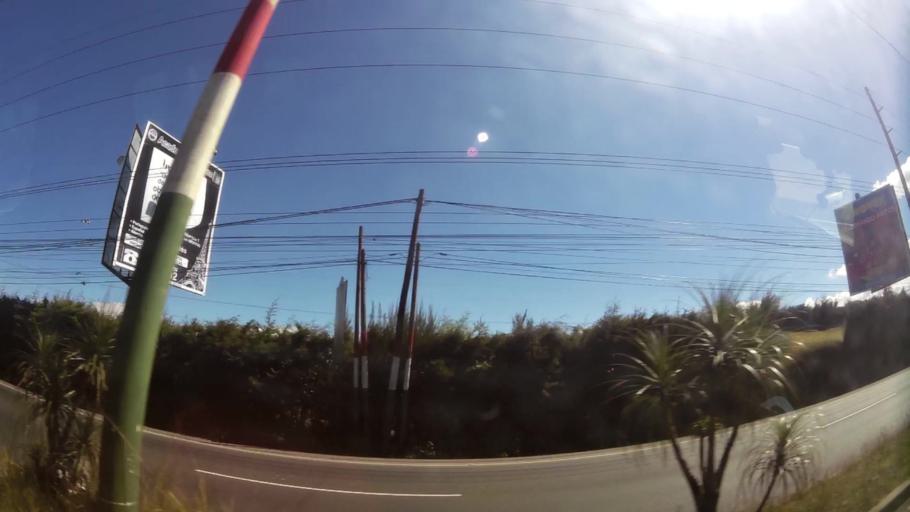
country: GT
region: Guatemala
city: Santa Catarina Pinula
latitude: 14.5164
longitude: -90.4737
